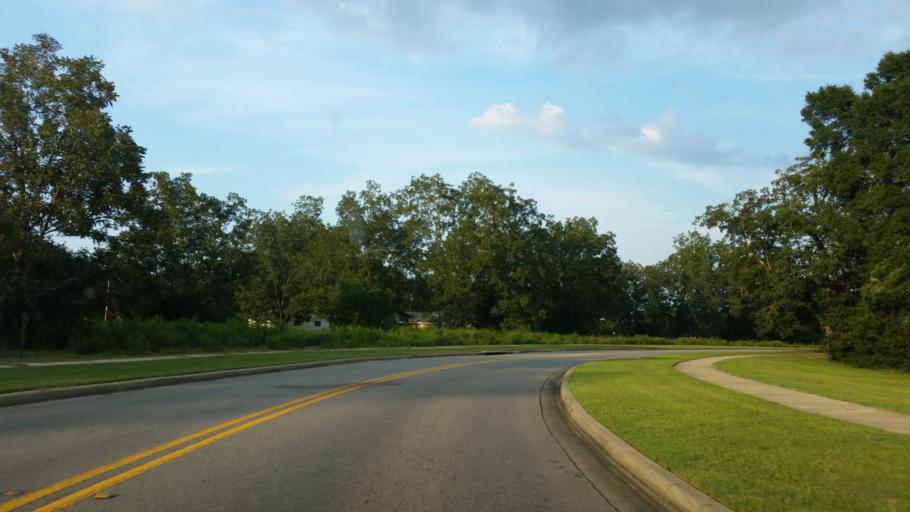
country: US
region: Florida
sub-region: Santa Rosa County
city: Pace
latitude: 30.5995
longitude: -87.1132
